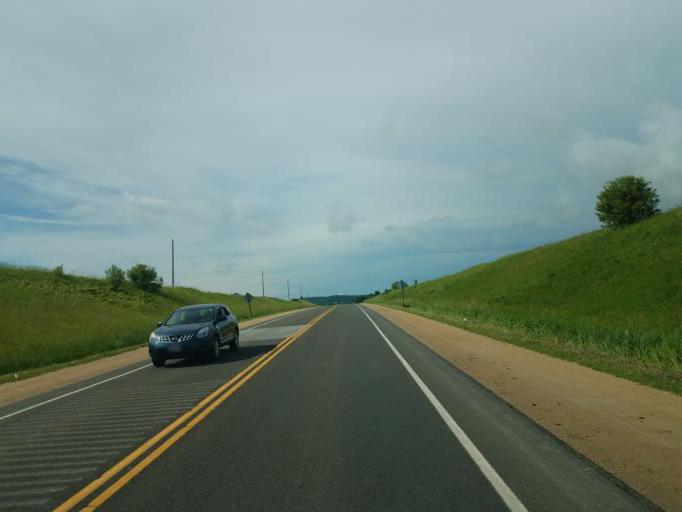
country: US
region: Wisconsin
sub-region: Monroe County
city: Tomah
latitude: 43.8345
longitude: -90.4739
